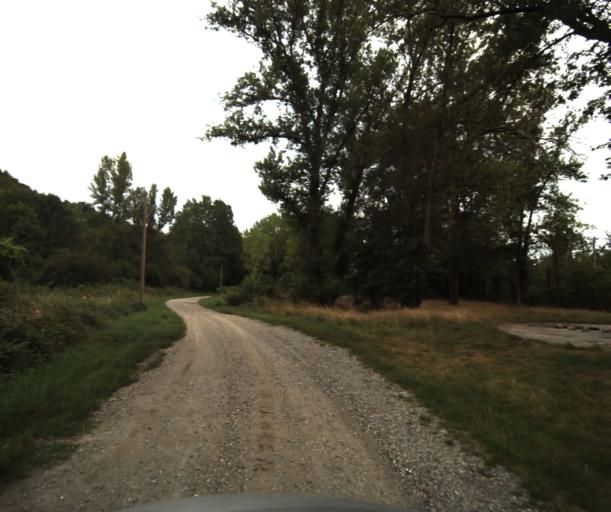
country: FR
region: Midi-Pyrenees
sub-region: Departement de la Haute-Garonne
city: Le Fauga
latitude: 43.4057
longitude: 1.3087
